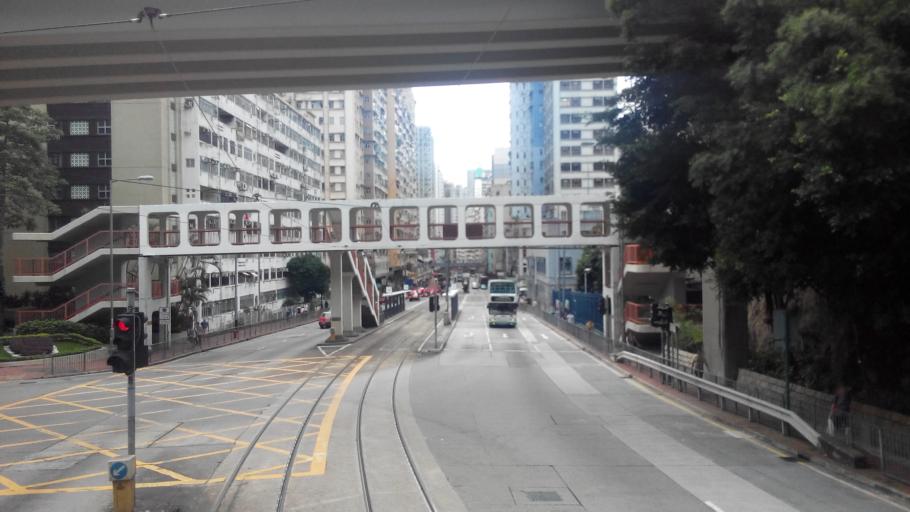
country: HK
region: Wanchai
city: Wan Chai
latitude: 22.2846
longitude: 114.2199
